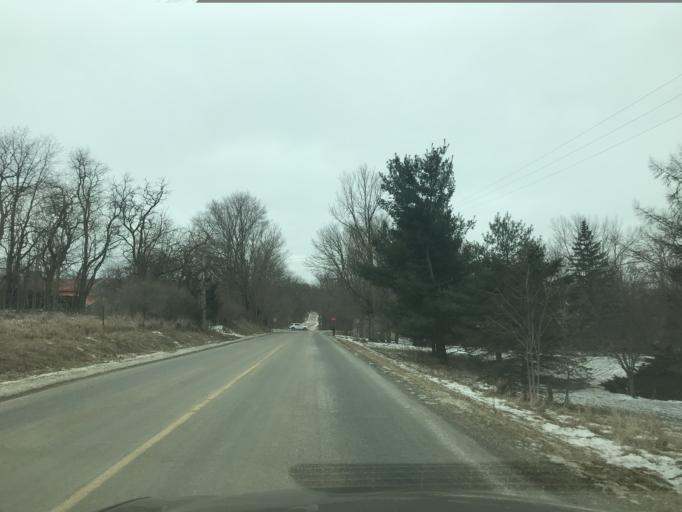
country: US
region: Michigan
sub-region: Lenawee County
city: Manitou Beach-Devils Lake
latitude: 42.0503
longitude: -84.3258
